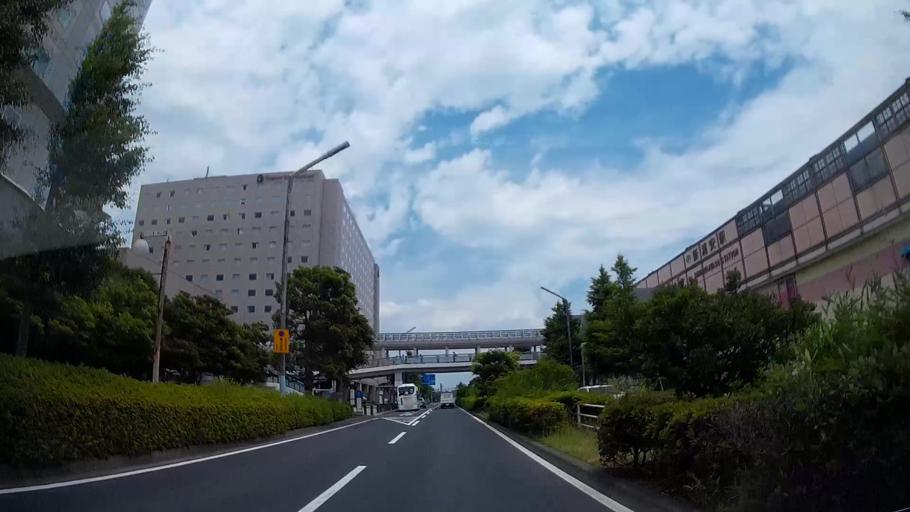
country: JP
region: Tokyo
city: Urayasu
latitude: 35.6497
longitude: 139.9120
